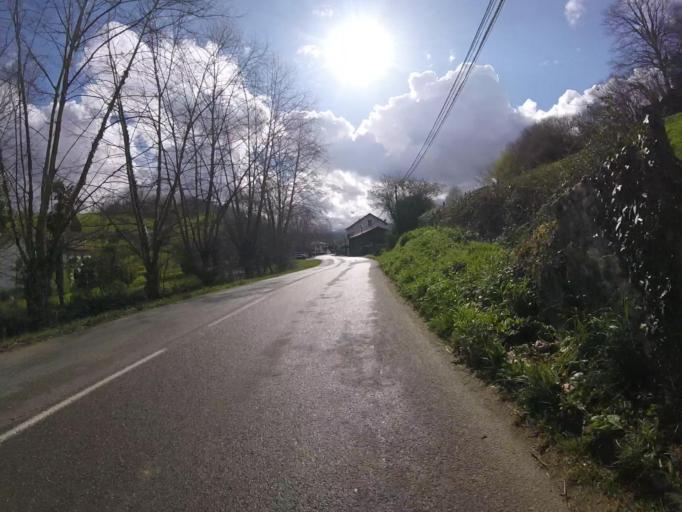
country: FR
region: Aquitaine
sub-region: Departement des Pyrenees-Atlantiques
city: Sare
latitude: 43.3019
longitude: -1.5742
